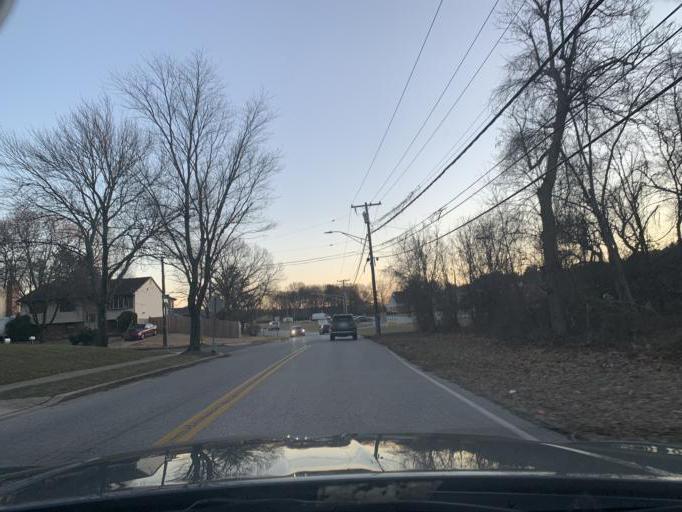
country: US
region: Maryland
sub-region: Anne Arundel County
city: Glen Burnie
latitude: 39.1573
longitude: -76.6428
